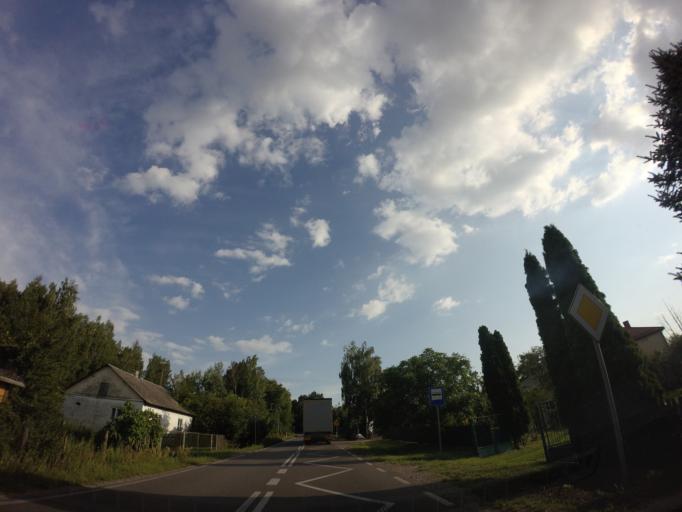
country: PL
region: Lublin Voivodeship
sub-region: Powiat lubartowski
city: Jeziorzany
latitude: 51.5895
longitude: 22.2829
